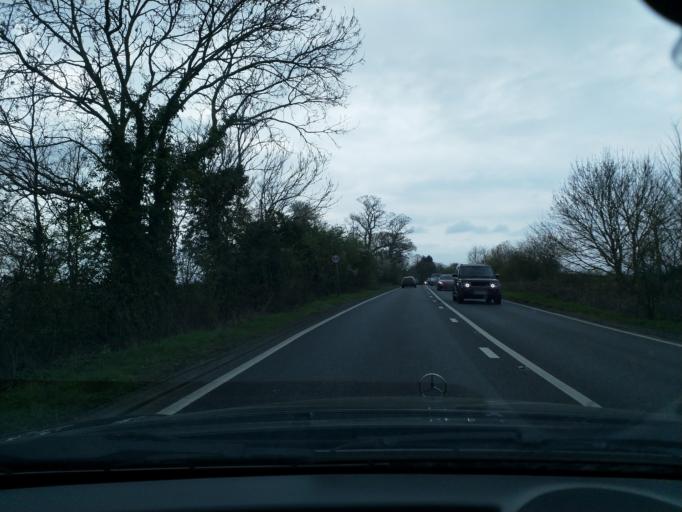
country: GB
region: England
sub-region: Warwickshire
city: Stratford-upon-Avon
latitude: 52.2355
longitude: -1.6542
